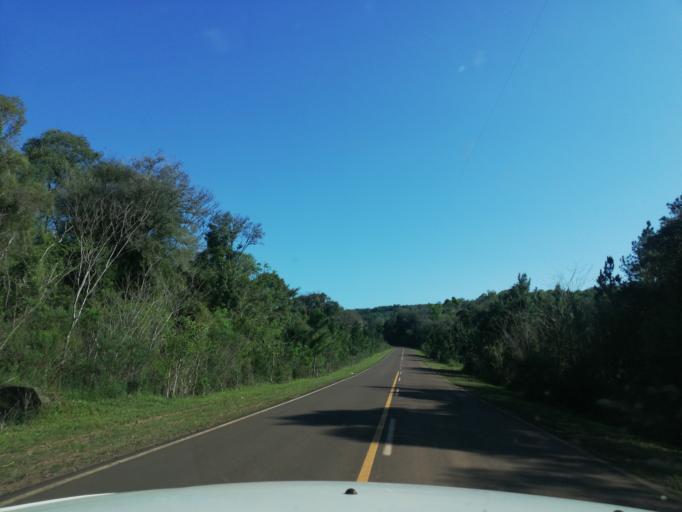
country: AR
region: Misiones
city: Arroyo del Medio
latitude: -27.6672
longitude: -55.3994
